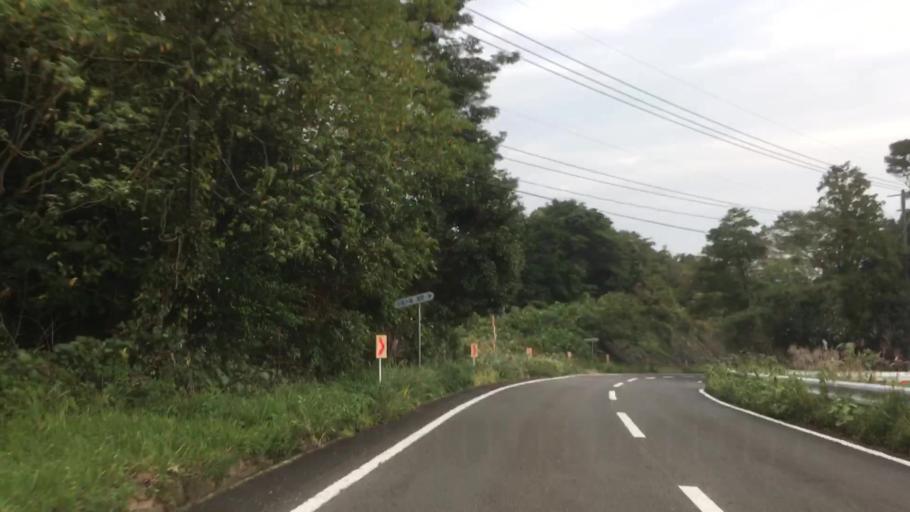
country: JP
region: Nagasaki
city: Sasebo
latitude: 33.0358
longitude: 129.6854
